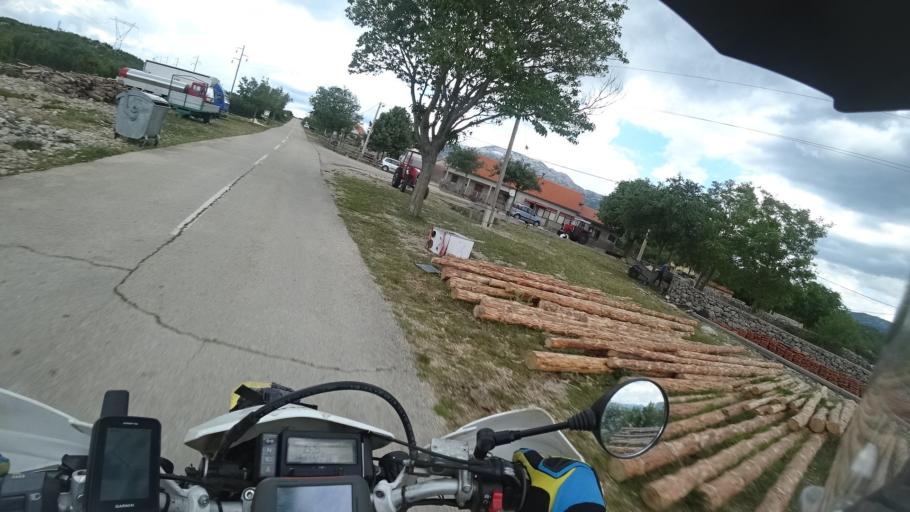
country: HR
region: Zadarska
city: Gracac
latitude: 44.2027
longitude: 15.8590
